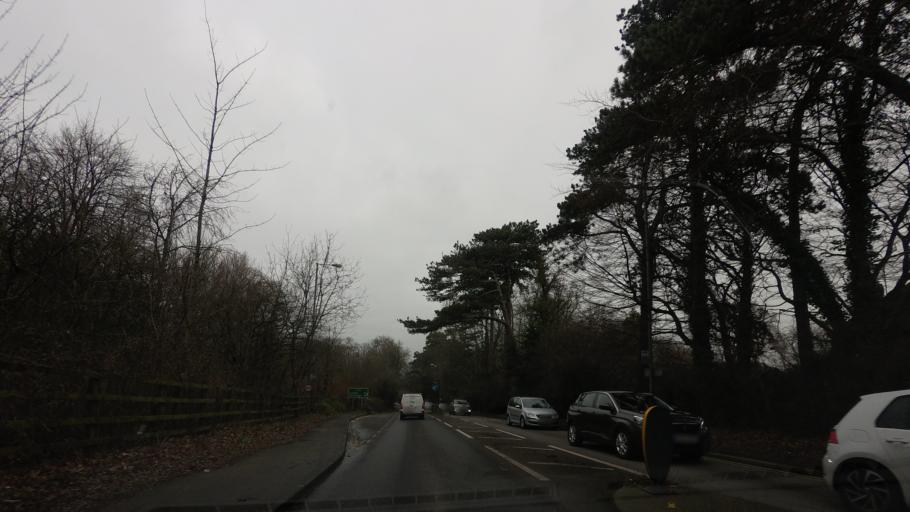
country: GB
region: England
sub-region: East Sussex
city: Saint Leonards-on-Sea
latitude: 50.8926
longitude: 0.5562
